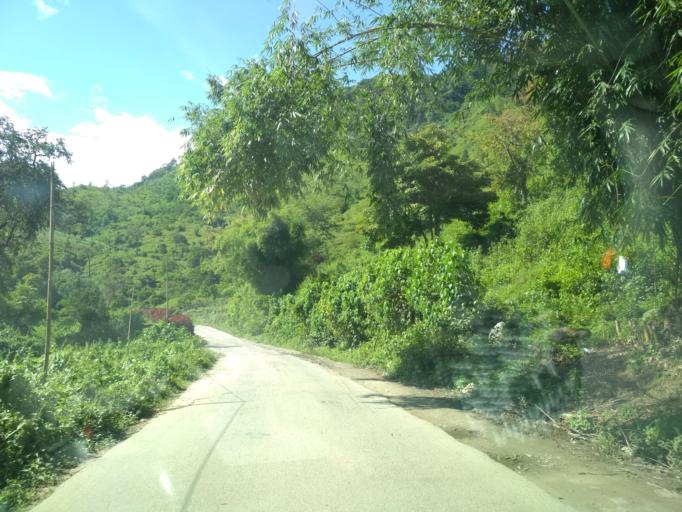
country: IN
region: Arunachal Pradesh
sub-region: Lower Subansiri
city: Ziro
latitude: 27.3620
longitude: 93.7787
